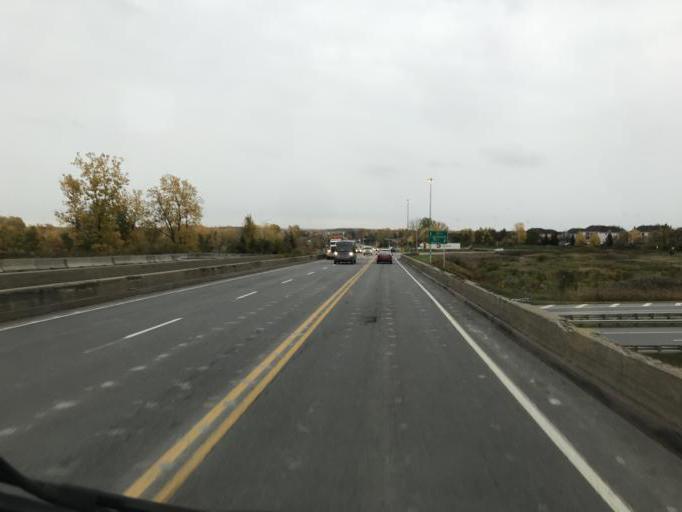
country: CA
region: Quebec
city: Bois-des-Filion
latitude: 45.6727
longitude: -73.7654
